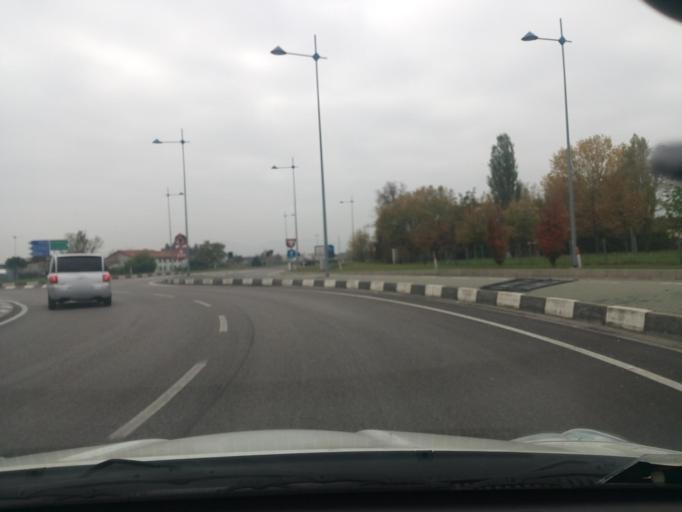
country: IT
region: Veneto
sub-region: Provincia di Vicenza
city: Thiene
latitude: 45.6878
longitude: 11.4700
